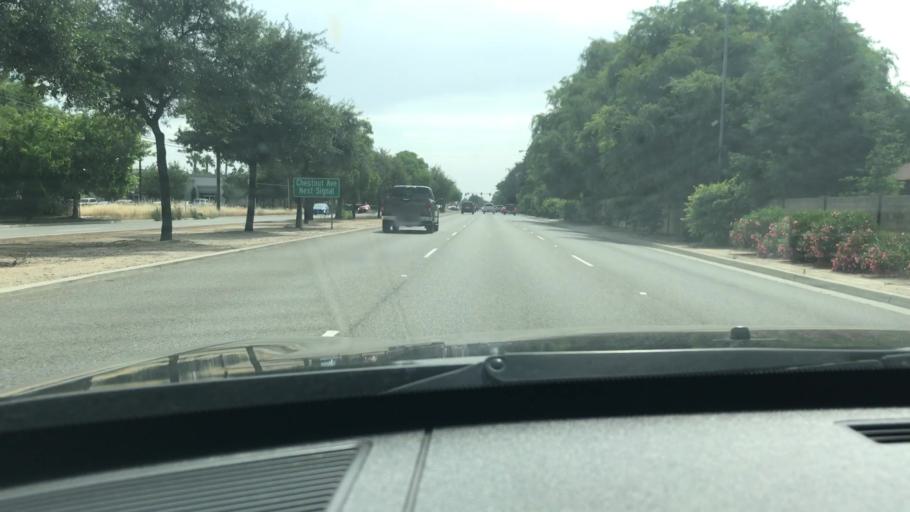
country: US
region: California
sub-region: Fresno County
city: Clovis
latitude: 36.8375
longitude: -119.7401
